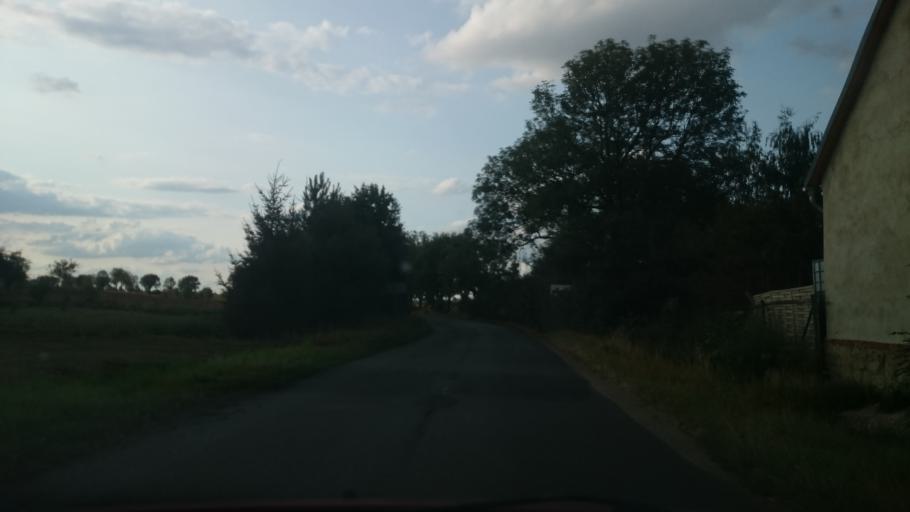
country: PL
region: Opole Voivodeship
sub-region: Powiat nyski
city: Otmuchow
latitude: 50.5035
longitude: 17.1962
